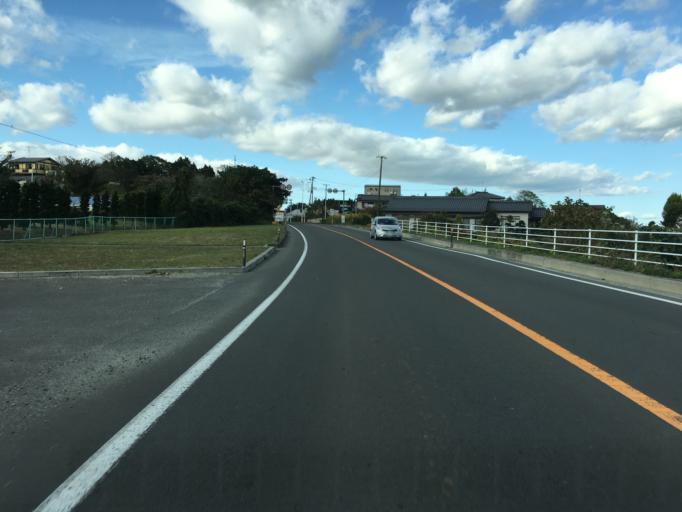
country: JP
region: Miyagi
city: Watari
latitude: 37.9137
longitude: 140.9044
